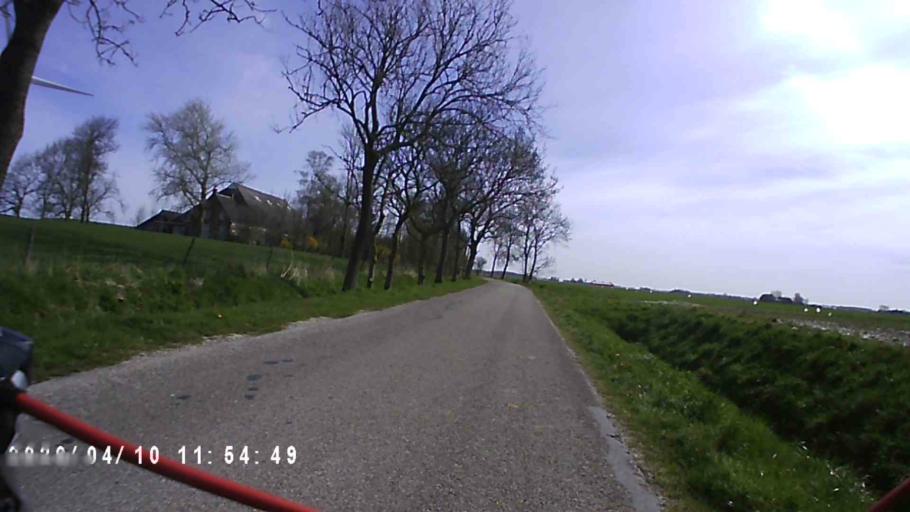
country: NL
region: Groningen
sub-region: Gemeente De Marne
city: Ulrum
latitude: 53.3857
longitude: 6.3384
